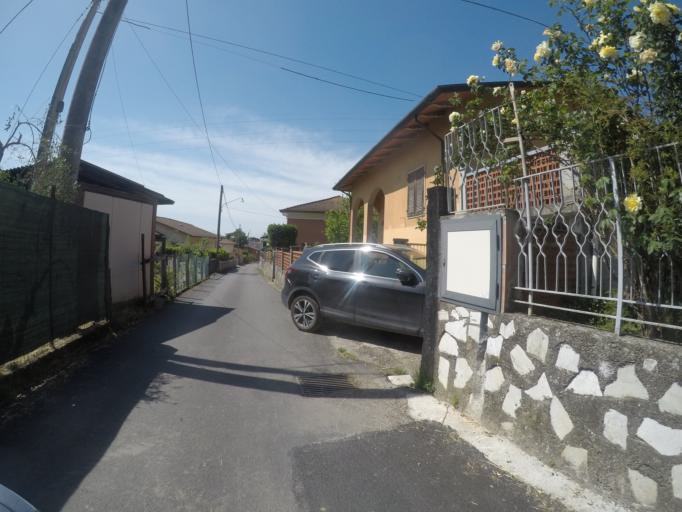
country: IT
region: Tuscany
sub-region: Provincia di Massa-Carrara
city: Carrara
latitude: 44.0440
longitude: 10.0909
